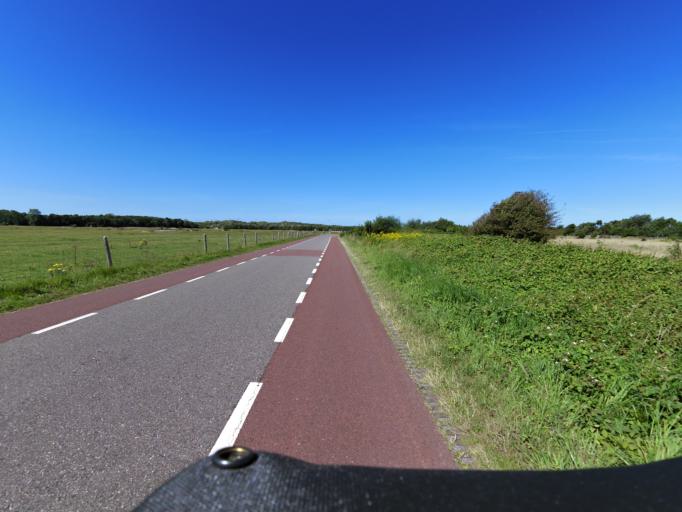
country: NL
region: Zeeland
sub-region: Schouwen-Duiveland
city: Haamstede
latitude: 51.7159
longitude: 3.7217
